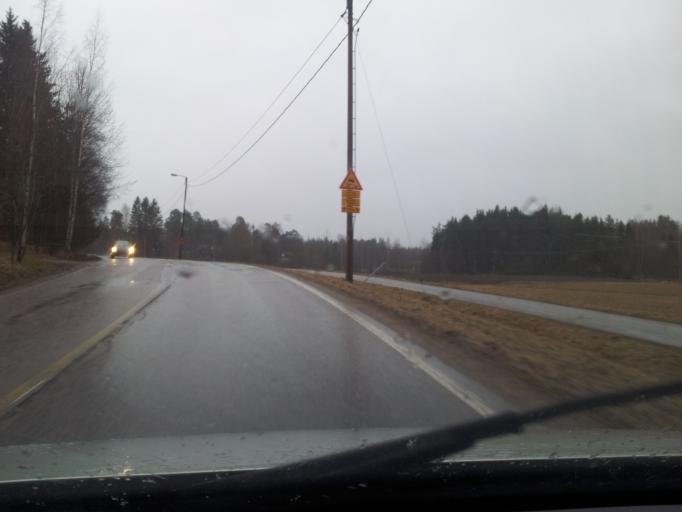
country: FI
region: Uusimaa
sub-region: Helsinki
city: Espoo
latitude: 60.1790
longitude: 24.5475
